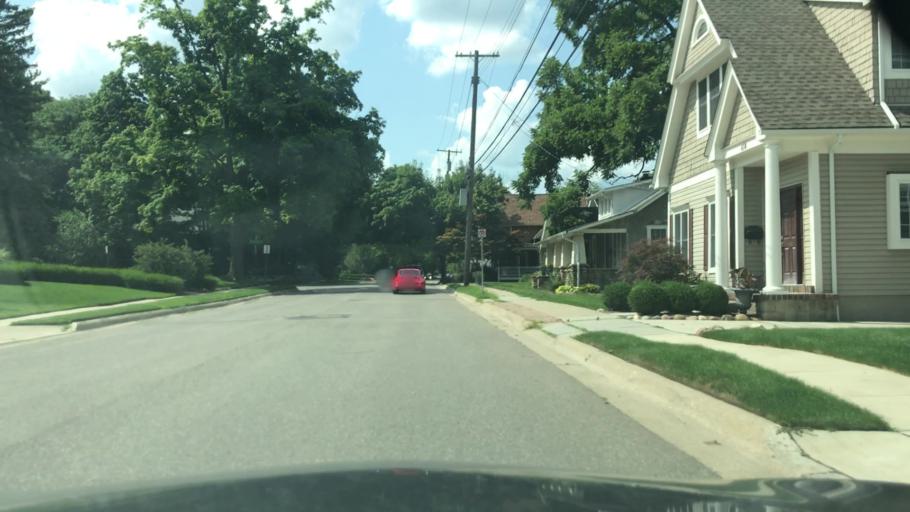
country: US
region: Michigan
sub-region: Wayne County
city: Northville
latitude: 42.4341
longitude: -83.4872
